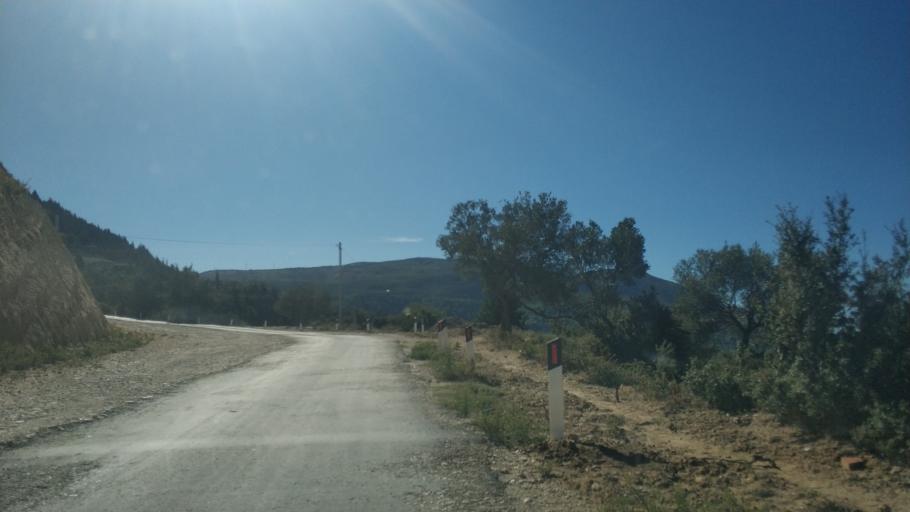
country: AL
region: Vlore
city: Vlore
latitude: 40.4490
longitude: 19.5159
